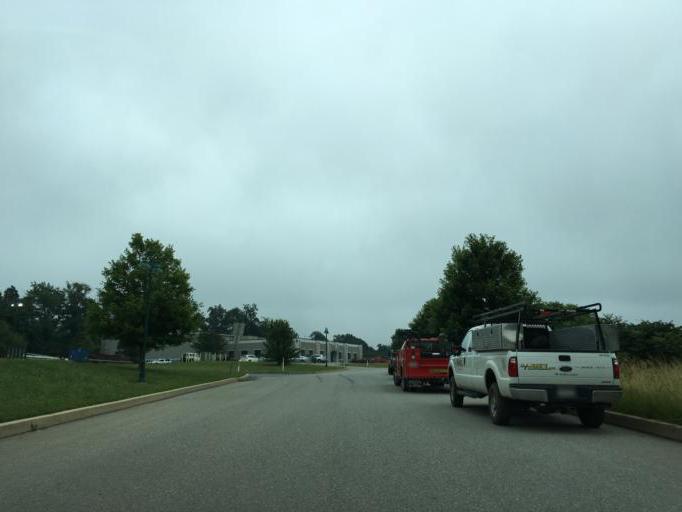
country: US
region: Pennsylvania
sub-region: York County
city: Shrewsbury
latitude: 39.7737
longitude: -76.6579
